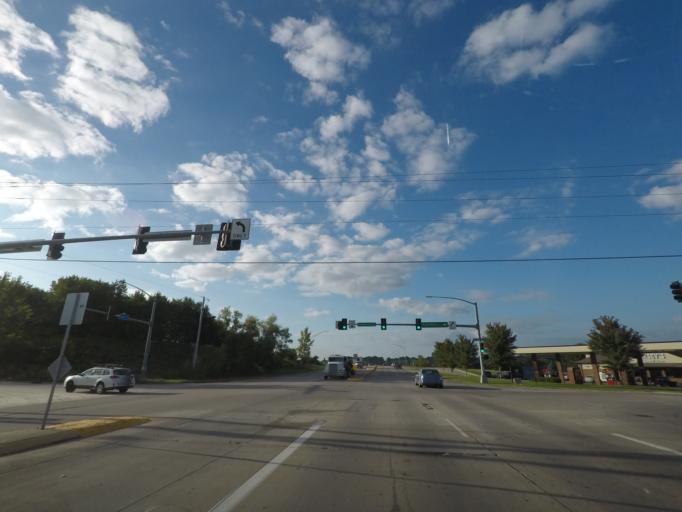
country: US
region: Iowa
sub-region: Warren County
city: Norwalk
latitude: 41.5124
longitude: -93.6450
